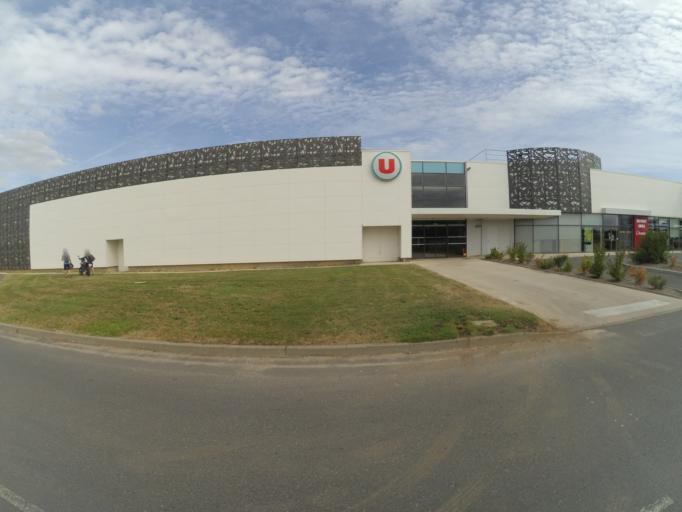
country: FR
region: Pays de la Loire
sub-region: Departement de Maine-et-Loire
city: Doue-la-Fontaine
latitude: 47.1914
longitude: -0.2904
